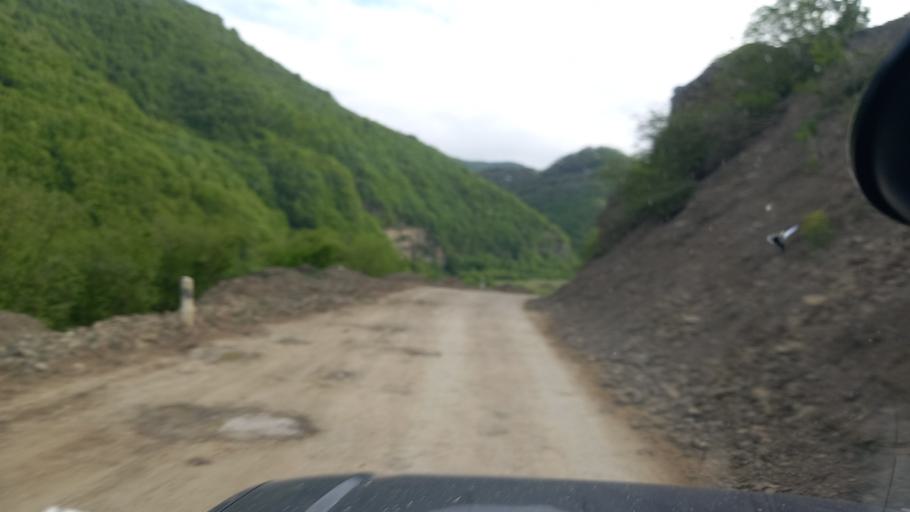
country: RU
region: Dagestan
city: Khuchni
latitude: 41.9664
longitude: 47.8739
